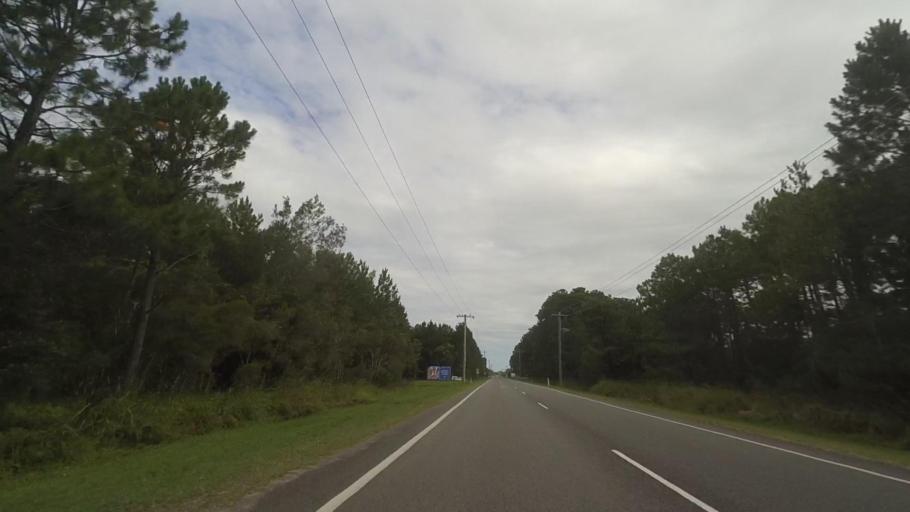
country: AU
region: New South Wales
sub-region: Great Lakes
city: Hawks Nest
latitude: -32.6466
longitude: 152.1473
